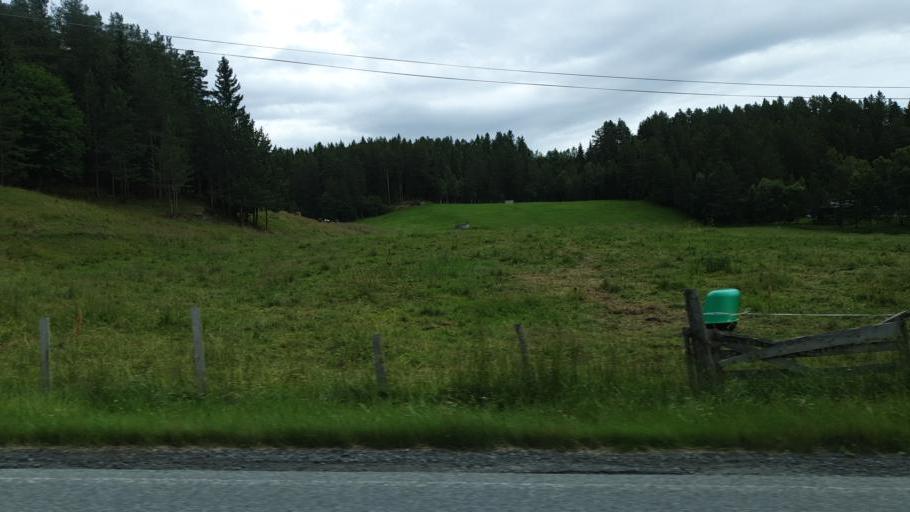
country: NO
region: Sor-Trondelag
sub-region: Rennebu
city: Berkak
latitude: 62.8661
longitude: 10.0700
